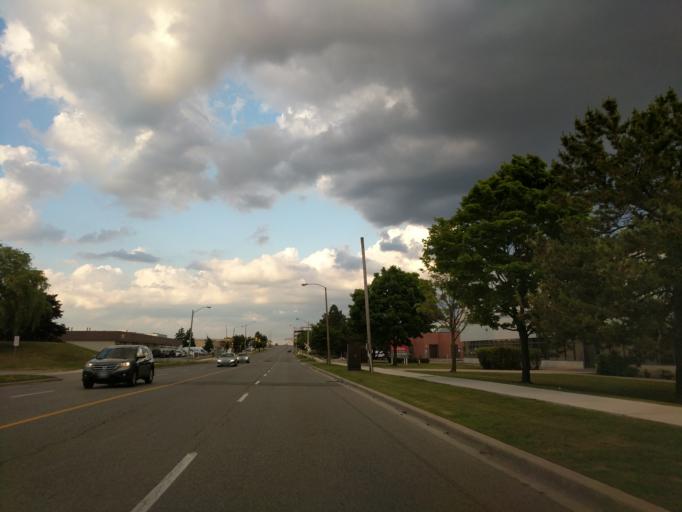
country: CA
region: Ontario
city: Markham
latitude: 43.8228
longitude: -79.2539
